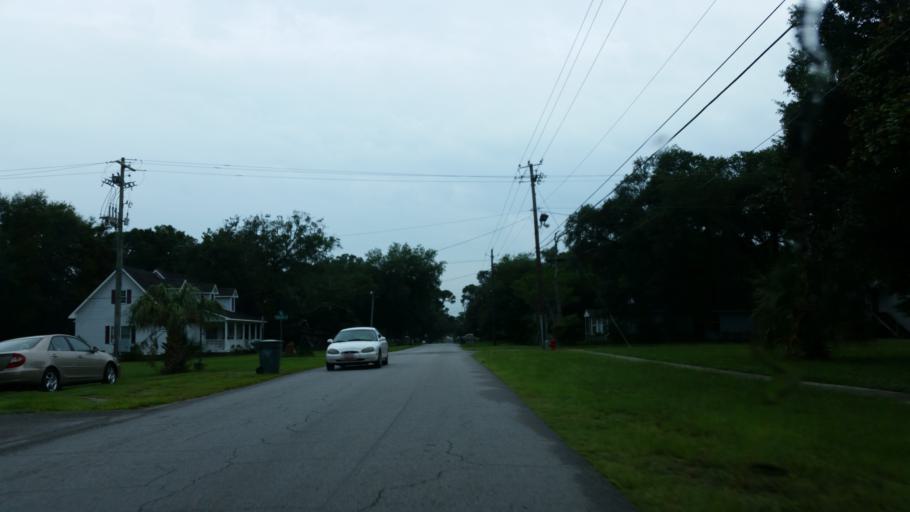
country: US
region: Florida
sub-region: Escambia County
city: Warrington
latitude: 30.3859
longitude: -87.2801
